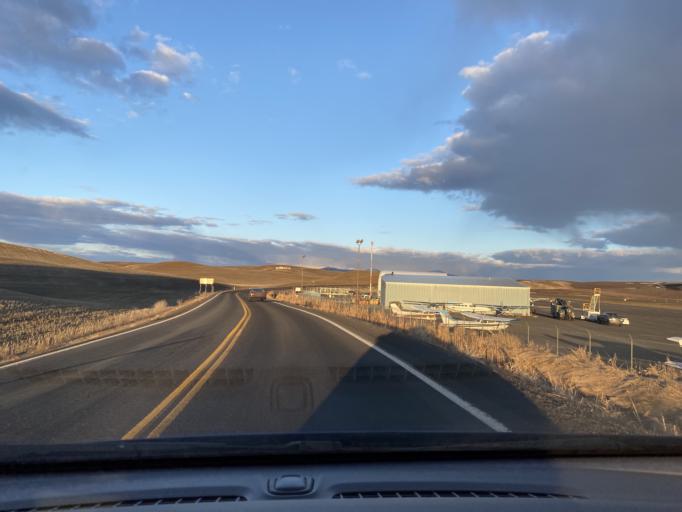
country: US
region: Washington
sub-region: Whitman County
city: Pullman
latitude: 46.7452
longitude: -117.1106
